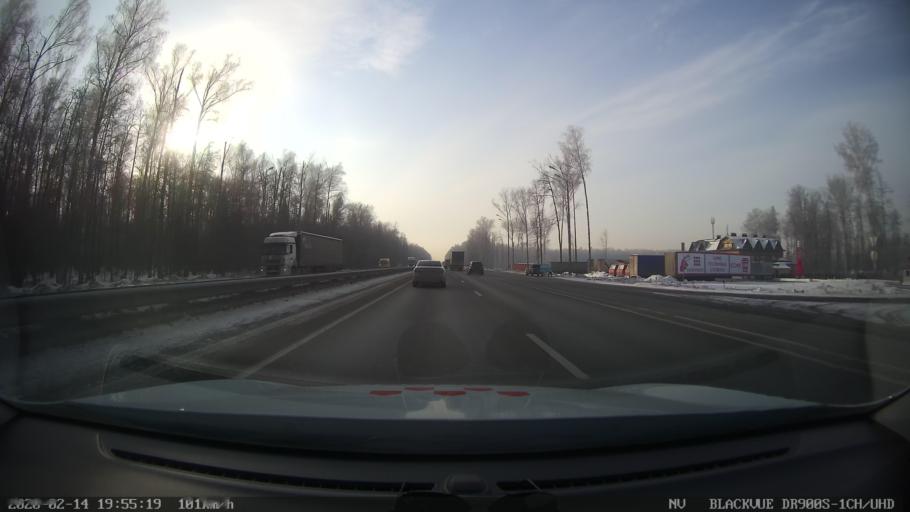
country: RU
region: Tatarstan
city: Osinovo
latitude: 55.8485
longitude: 48.8529
